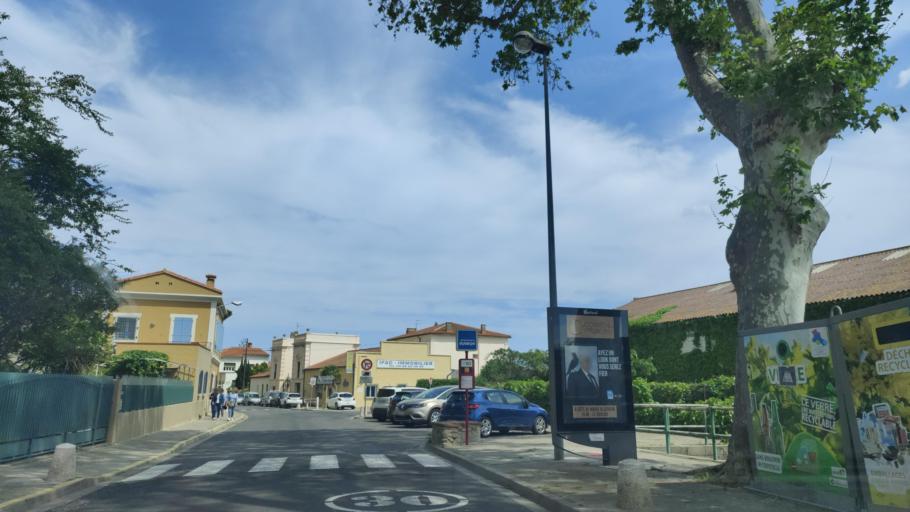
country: FR
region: Languedoc-Roussillon
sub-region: Departement des Pyrenees-Orientales
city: Elne
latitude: 42.5978
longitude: 2.9713
